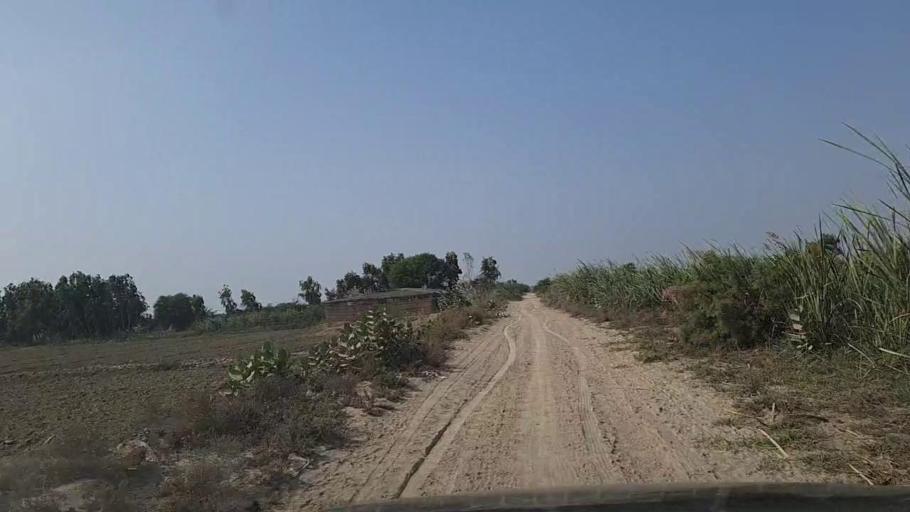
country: PK
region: Sindh
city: Gharo
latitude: 24.7314
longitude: 67.7292
